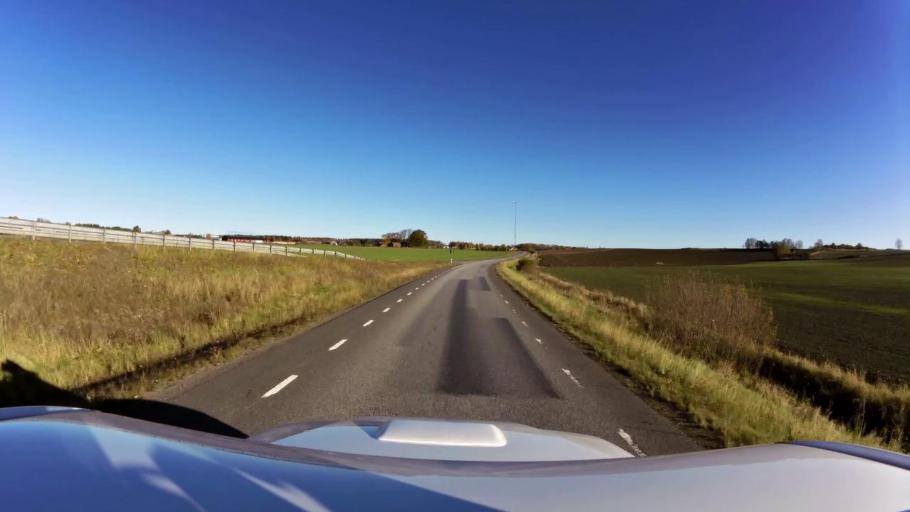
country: SE
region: OEstergoetland
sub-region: Linkopings Kommun
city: Ljungsbro
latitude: 58.4806
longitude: 15.4883
